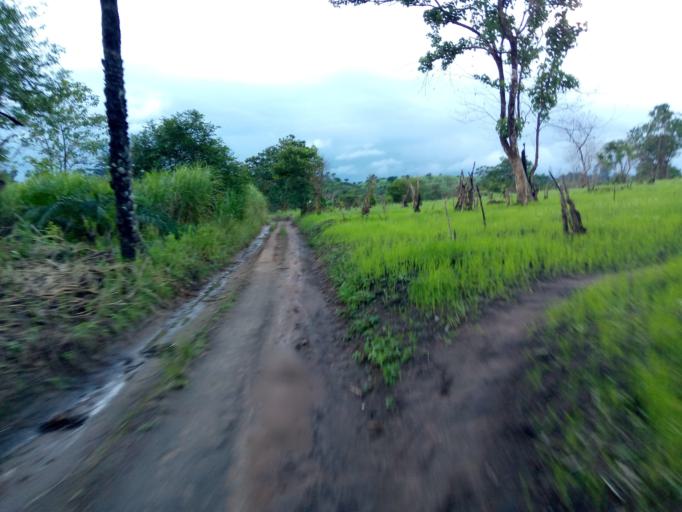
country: SL
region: Eastern Province
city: Buedu
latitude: 8.4907
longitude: -10.3435
